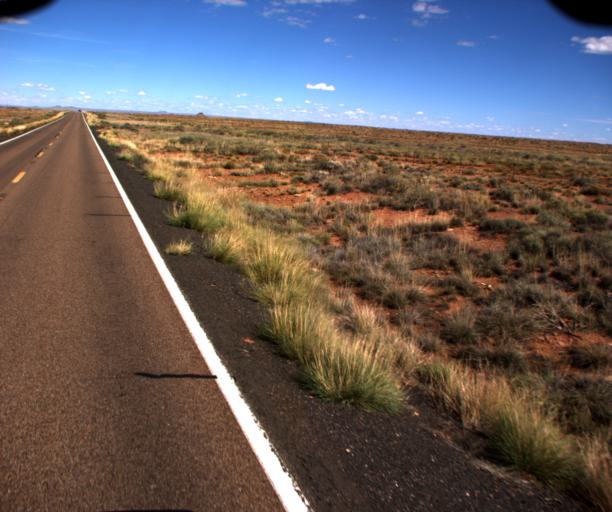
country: US
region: Arizona
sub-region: Navajo County
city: Holbrook
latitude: 34.8176
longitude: -110.1977
